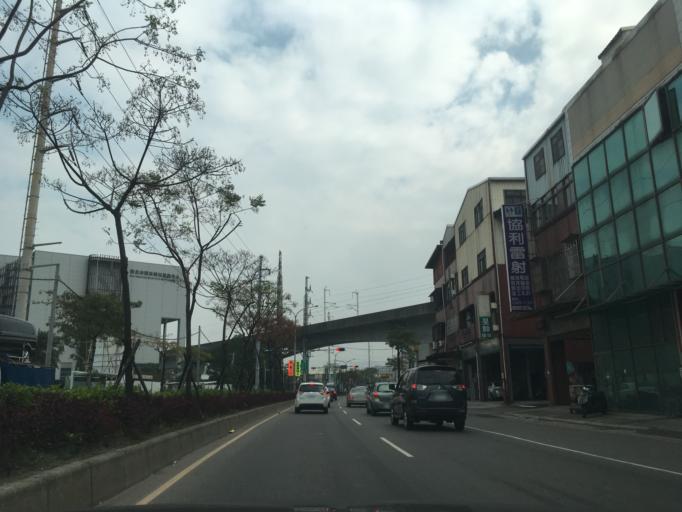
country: TW
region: Taipei
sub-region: Taipei
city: Banqiao
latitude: 25.0047
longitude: 121.4219
